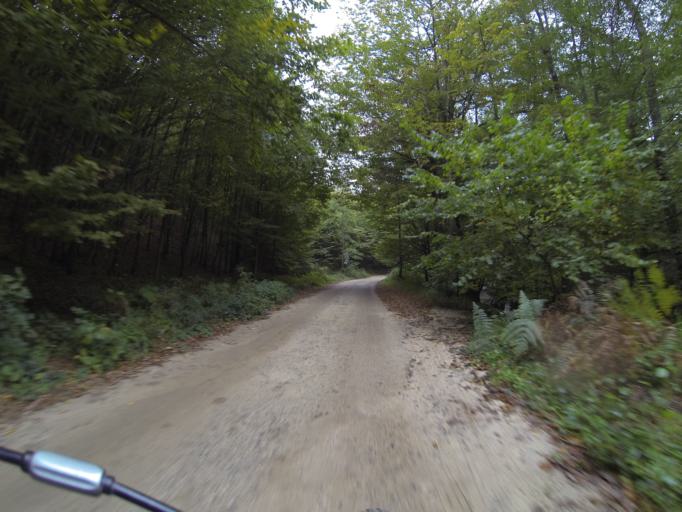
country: RO
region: Gorj
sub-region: Comuna Tismana
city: Sohodol
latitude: 45.0601
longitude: 22.8982
